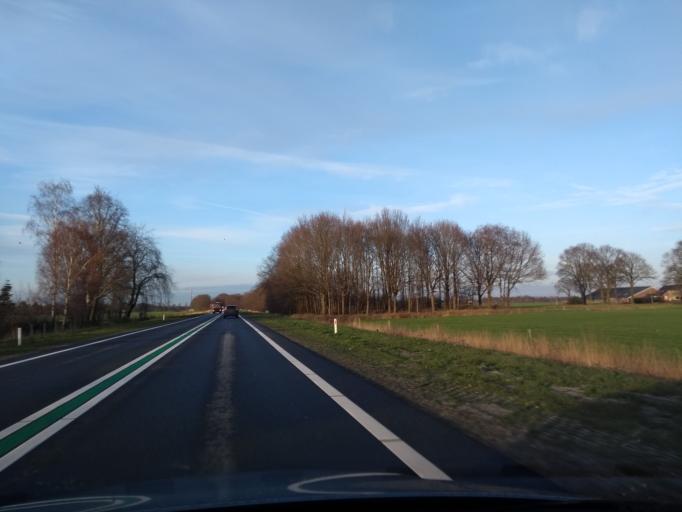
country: NL
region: Overijssel
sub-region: Gemeente Twenterand
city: Westerhaar-Vriezenveensewijk
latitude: 52.4448
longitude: 6.6288
